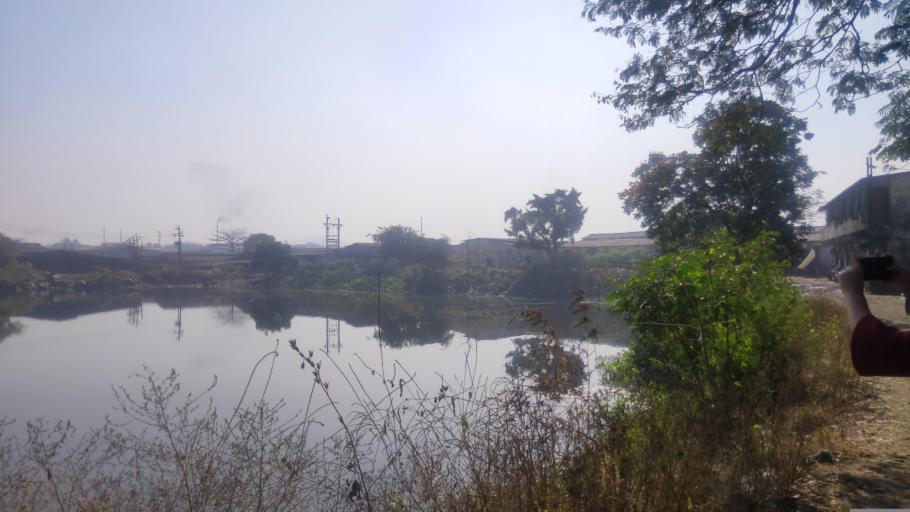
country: IN
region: Maharashtra
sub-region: Thane
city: Bhiwandi
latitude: 19.2938
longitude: 73.0350
